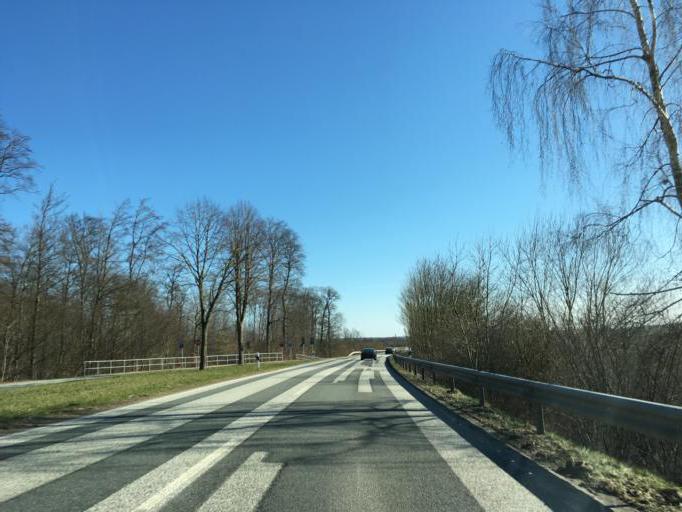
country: DE
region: Schleswig-Holstein
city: Kulpin
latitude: 53.7210
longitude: 10.6786
